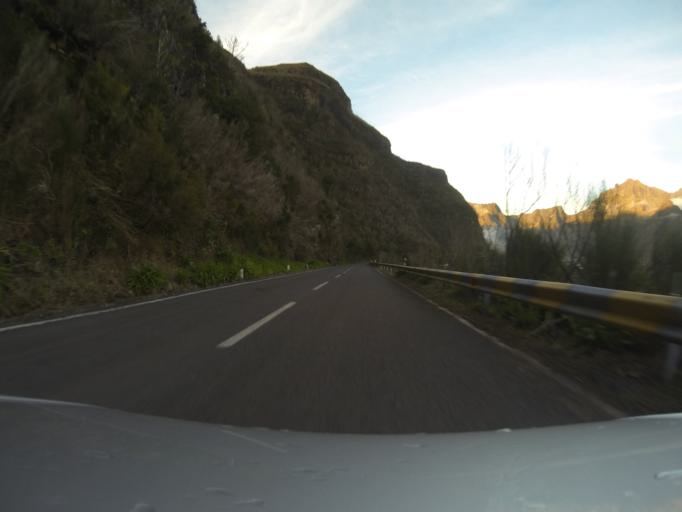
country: PT
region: Madeira
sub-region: Sao Vicente
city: Sao Vicente
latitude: 32.7527
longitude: -17.0280
